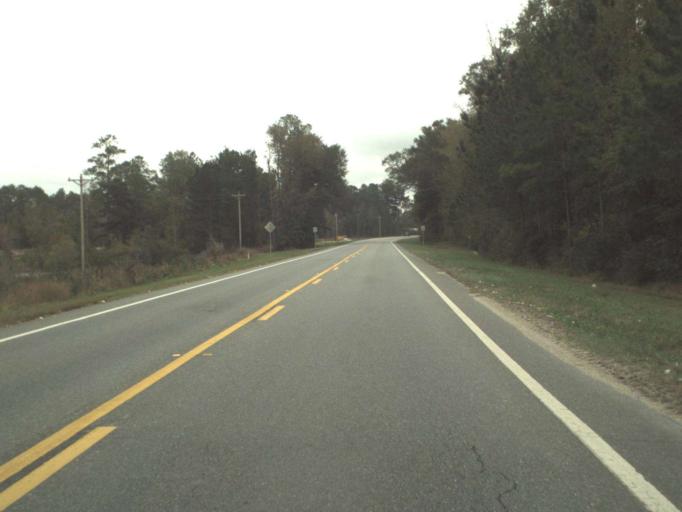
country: US
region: Florida
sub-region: Escambia County
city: Century
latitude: 30.9772
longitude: -87.2486
